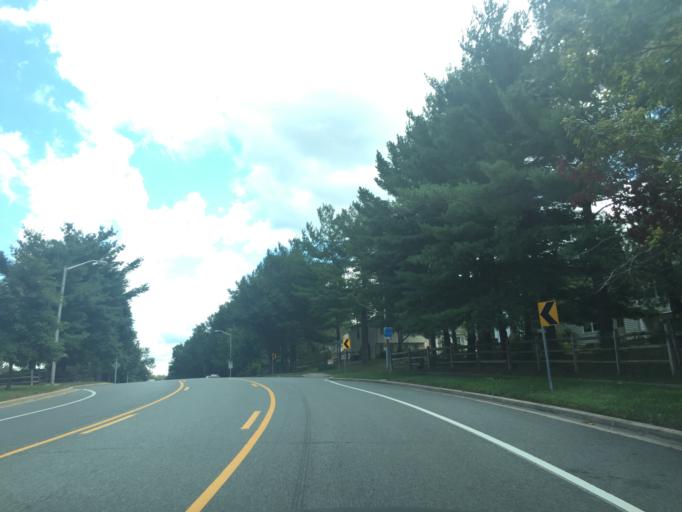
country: US
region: Maryland
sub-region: Montgomery County
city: Montgomery Village
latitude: 39.1695
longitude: -77.1836
